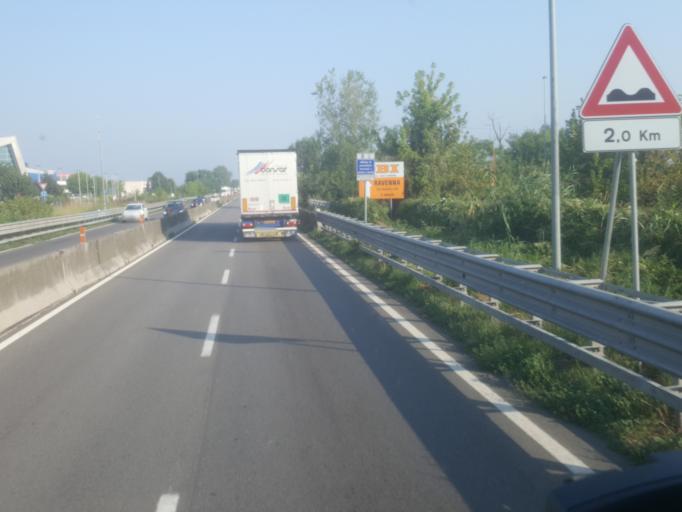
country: IT
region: Emilia-Romagna
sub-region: Provincia di Ravenna
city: Ravenna
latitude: 44.4130
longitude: 12.1710
